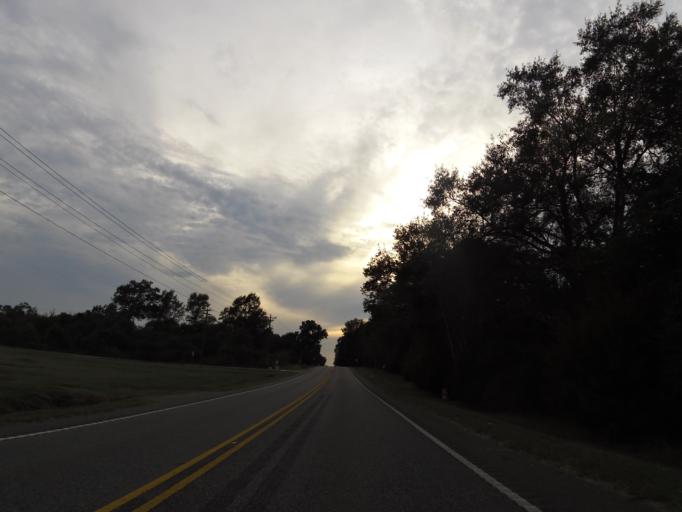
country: US
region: Alabama
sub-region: Escambia County
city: Atmore
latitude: 31.0227
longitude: -87.5295
